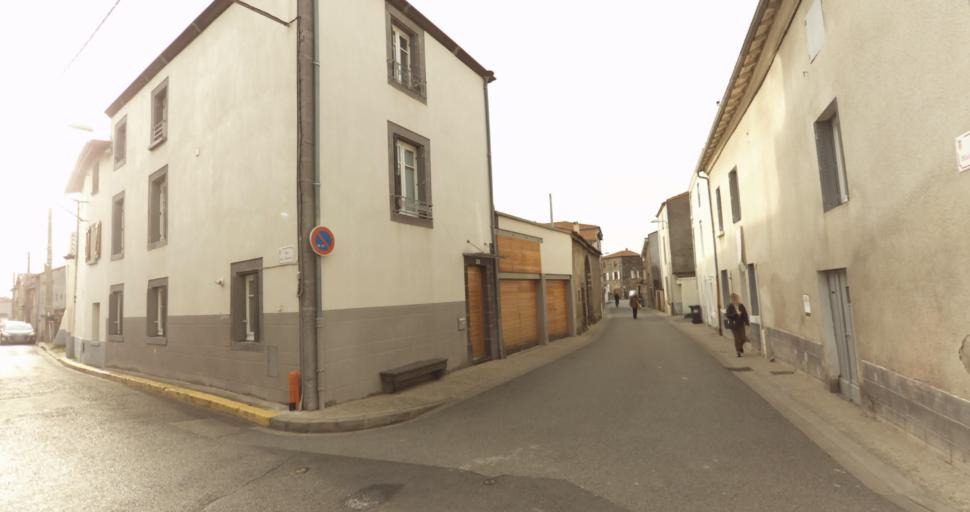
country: FR
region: Auvergne
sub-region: Departement du Puy-de-Dome
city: Cebazat
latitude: 45.8332
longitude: 3.0987
